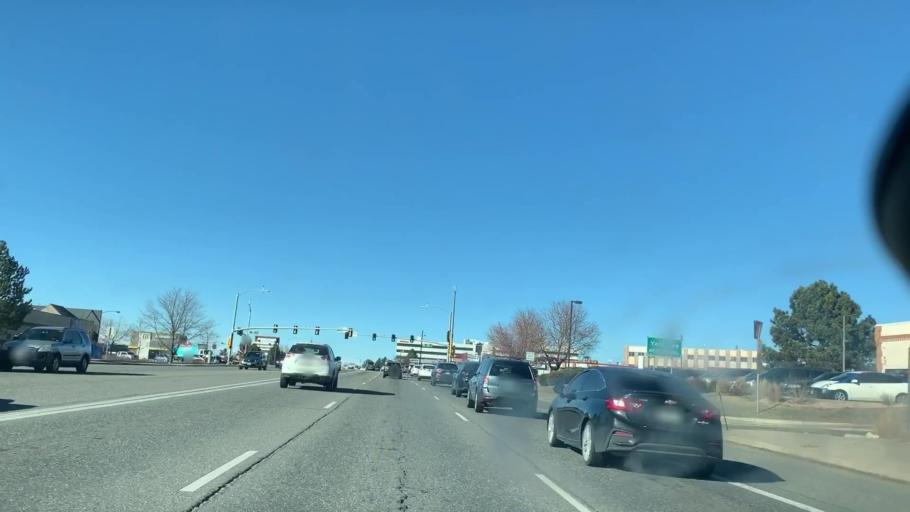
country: US
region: Colorado
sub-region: Adams County
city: Aurora
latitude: 39.6666
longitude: -104.8612
